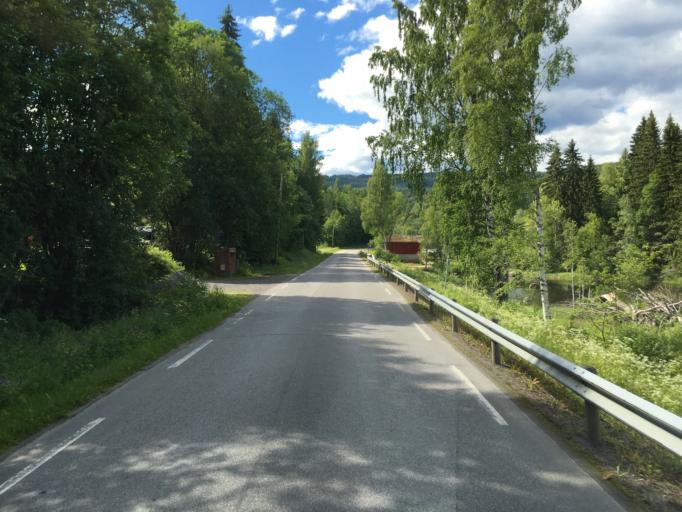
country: NO
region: Oppland
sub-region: Sondre Land
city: Hov
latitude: 60.5193
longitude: 10.2892
